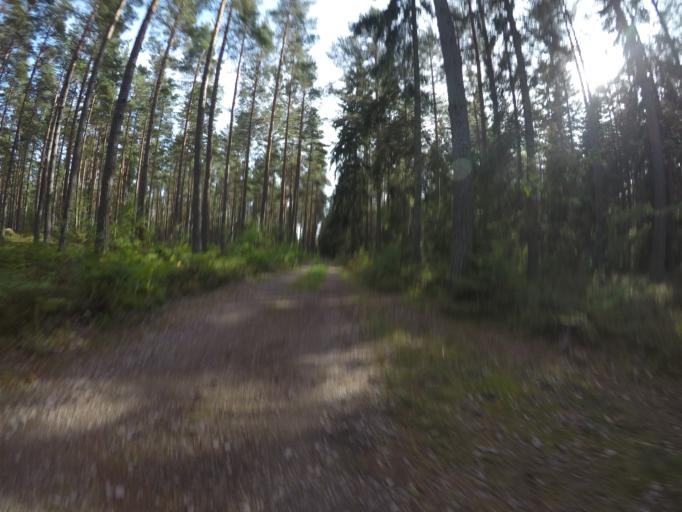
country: SE
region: Soedermanland
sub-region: Eskilstuna Kommun
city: Kvicksund
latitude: 59.5281
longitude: 16.3345
